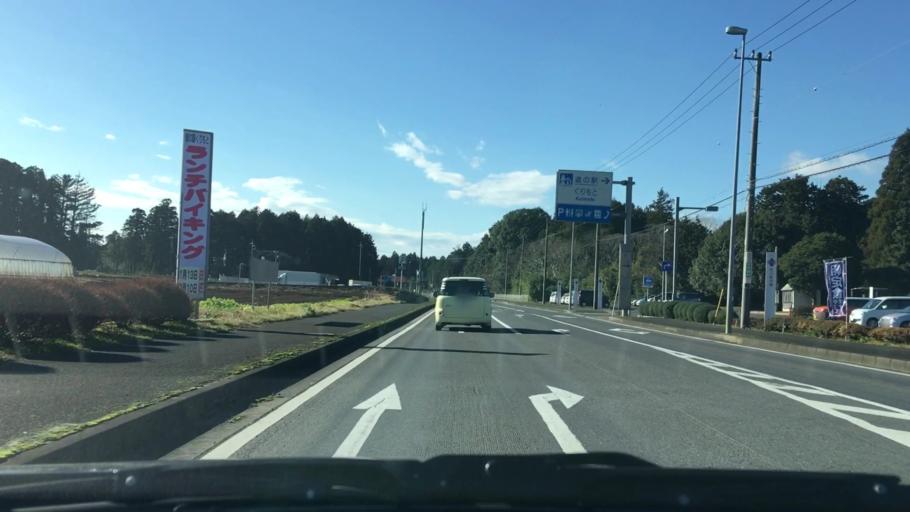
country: JP
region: Chiba
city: Sawara
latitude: 35.8058
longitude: 140.4707
